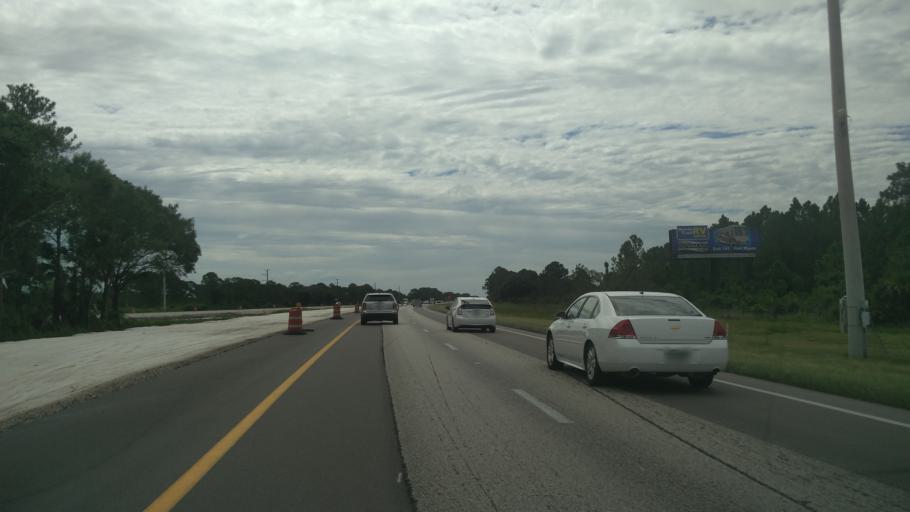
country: US
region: Florida
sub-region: Charlotte County
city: Port Charlotte
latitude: 27.0937
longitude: -82.1235
